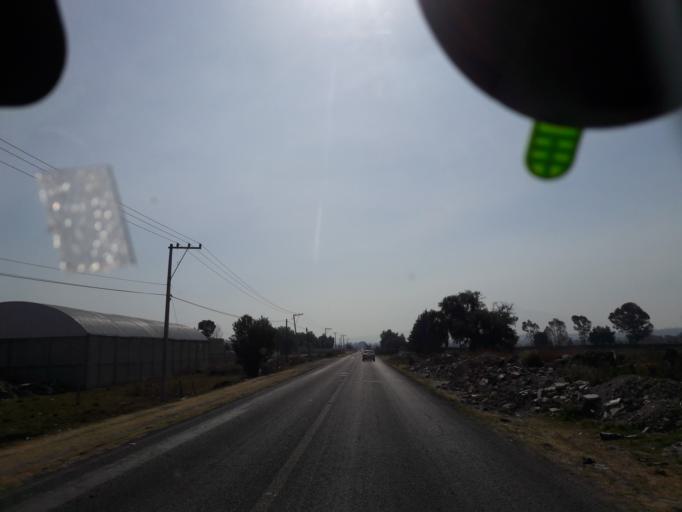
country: MX
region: Tlaxcala
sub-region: Panotla
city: Fraccionamiento la Virgen
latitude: 19.3214
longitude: -98.2987
